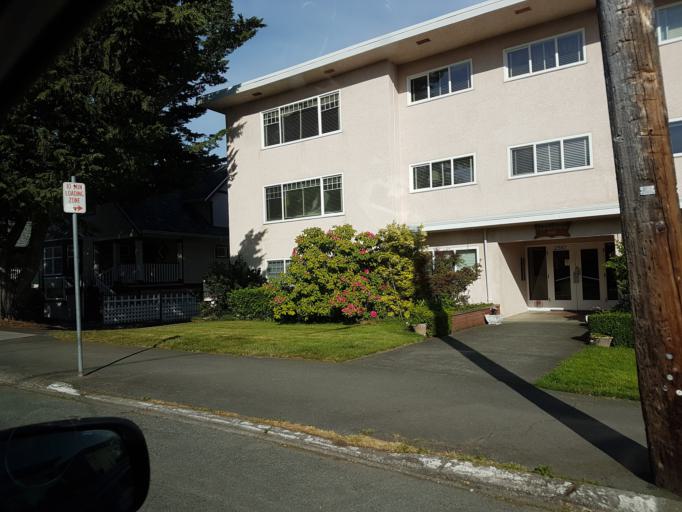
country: CA
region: British Columbia
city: Oak Bay
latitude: 48.4369
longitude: -123.3031
